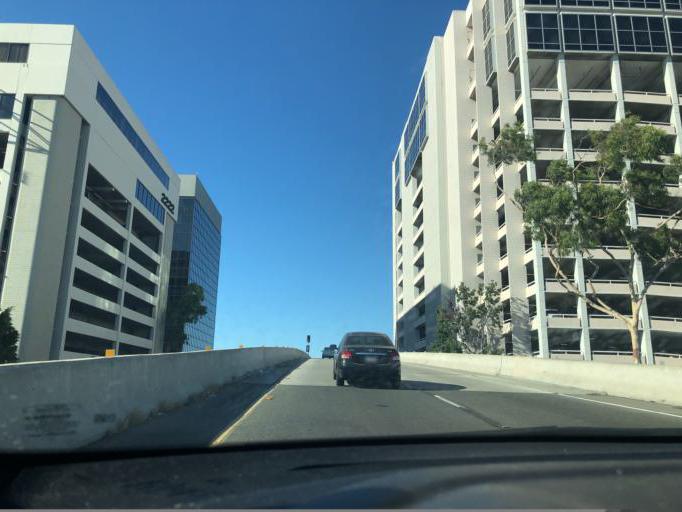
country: US
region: California
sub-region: Los Angeles County
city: Del Aire
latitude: 33.9291
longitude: -118.3852
